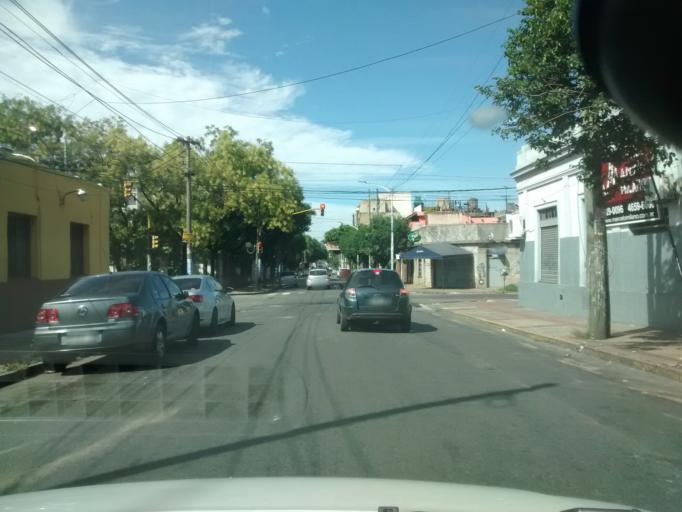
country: AR
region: Buenos Aires
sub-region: Partido de Moron
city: Moron
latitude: -34.6545
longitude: -58.6227
